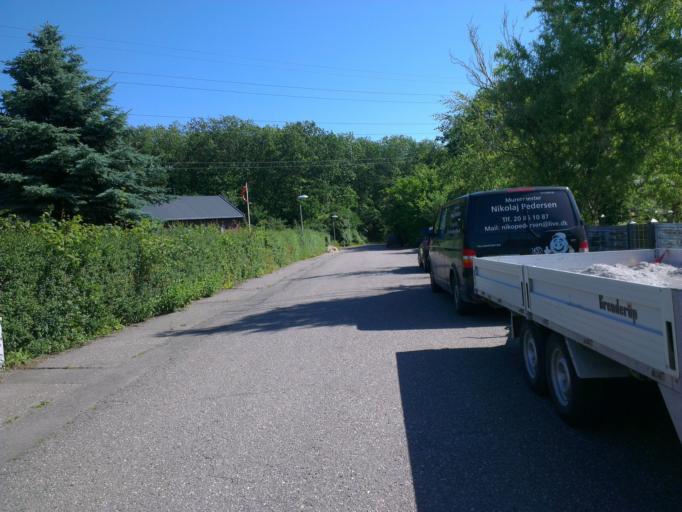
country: DK
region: Capital Region
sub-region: Frederikssund Kommune
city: Jaegerspris
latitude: 55.8109
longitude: 11.8880
